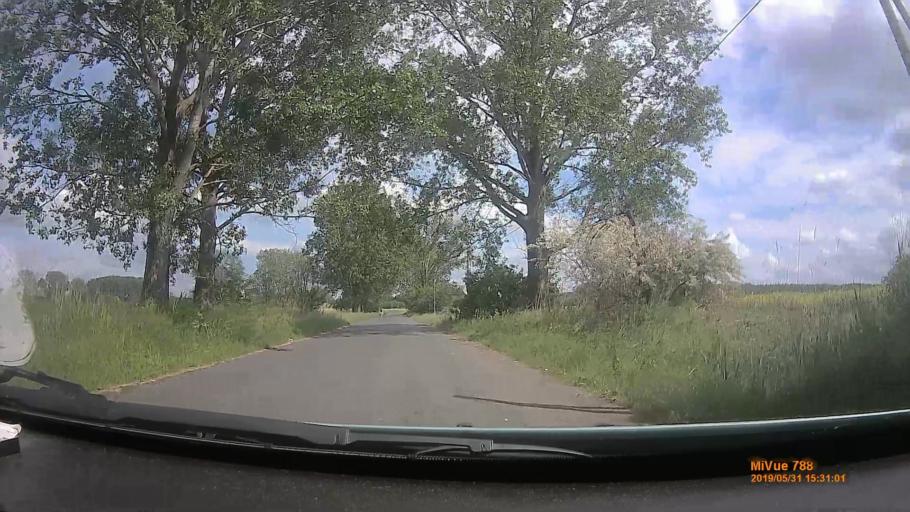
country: HU
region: Borsod-Abauj-Zemplen
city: Prugy
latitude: 48.0621
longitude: 21.2274
